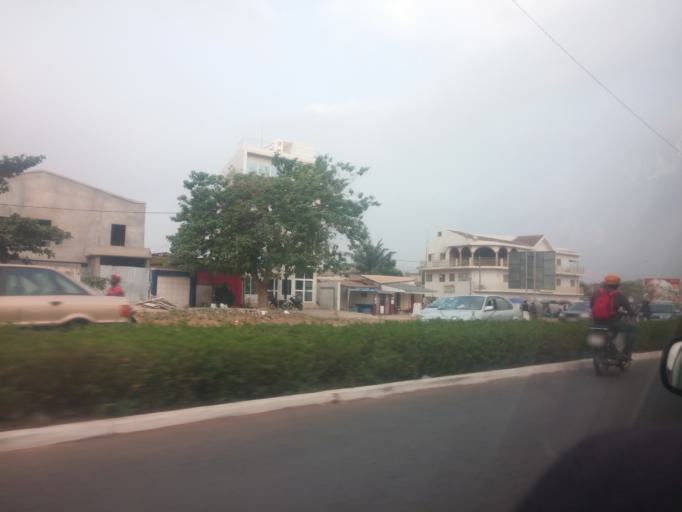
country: TG
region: Maritime
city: Lome
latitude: 6.1638
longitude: 1.2233
